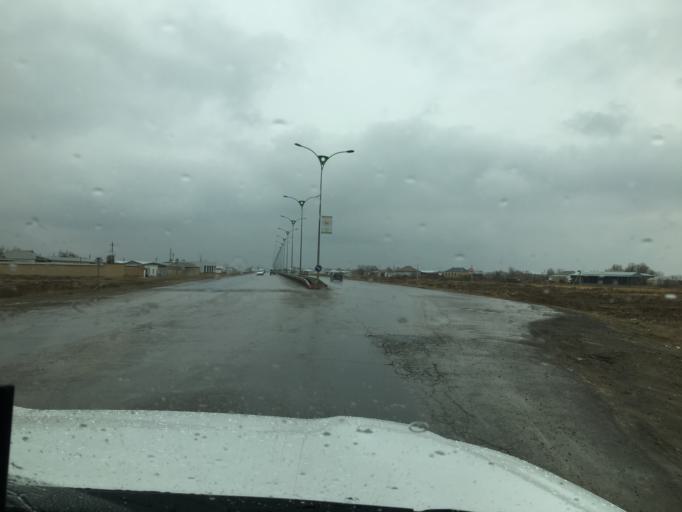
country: TM
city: Murgab
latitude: 37.4855
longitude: 61.9936
